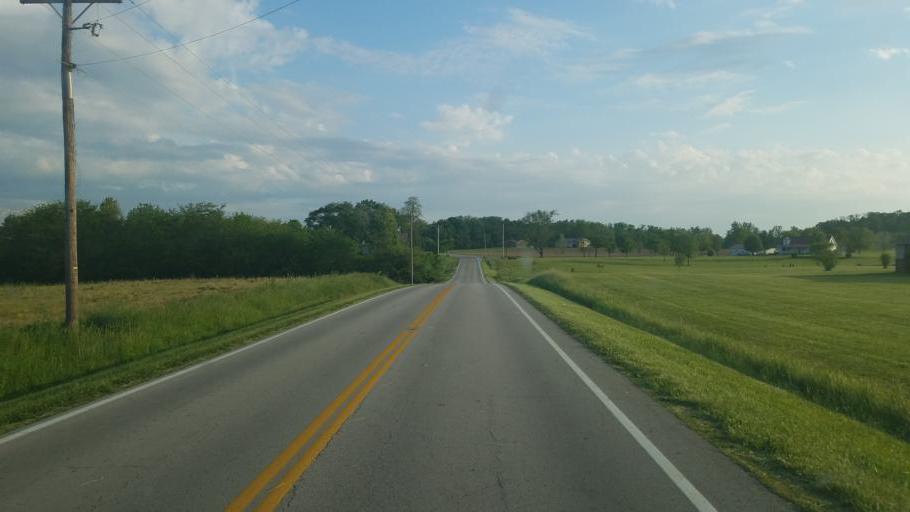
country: US
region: Ohio
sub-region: Highland County
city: Leesburg
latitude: 39.3870
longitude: -83.5947
